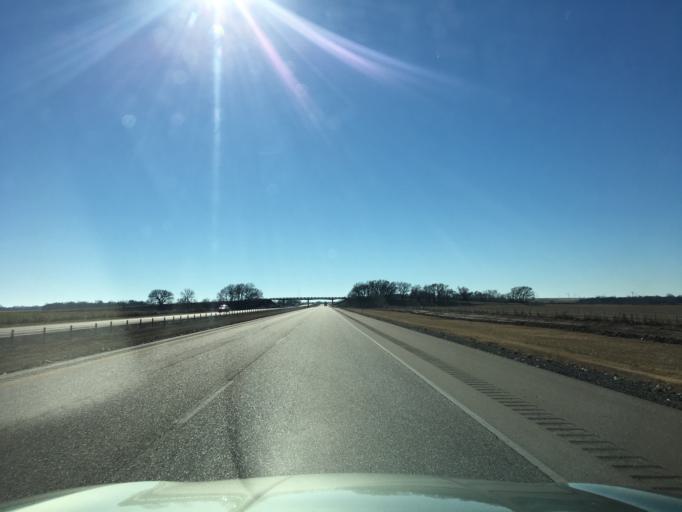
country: US
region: Oklahoma
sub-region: Kay County
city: Blackwell
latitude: 36.9164
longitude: -97.3514
